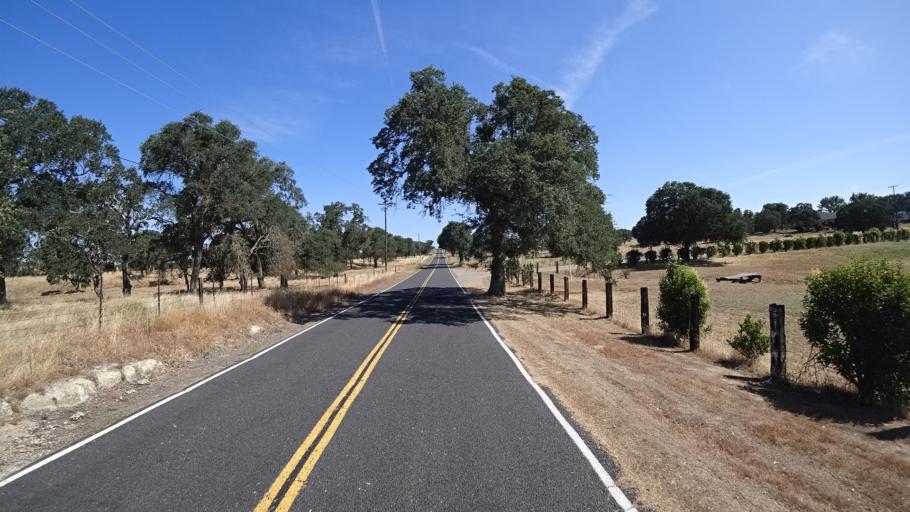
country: US
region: California
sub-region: Calaveras County
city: Rancho Calaveras
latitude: 38.1170
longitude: -120.9265
